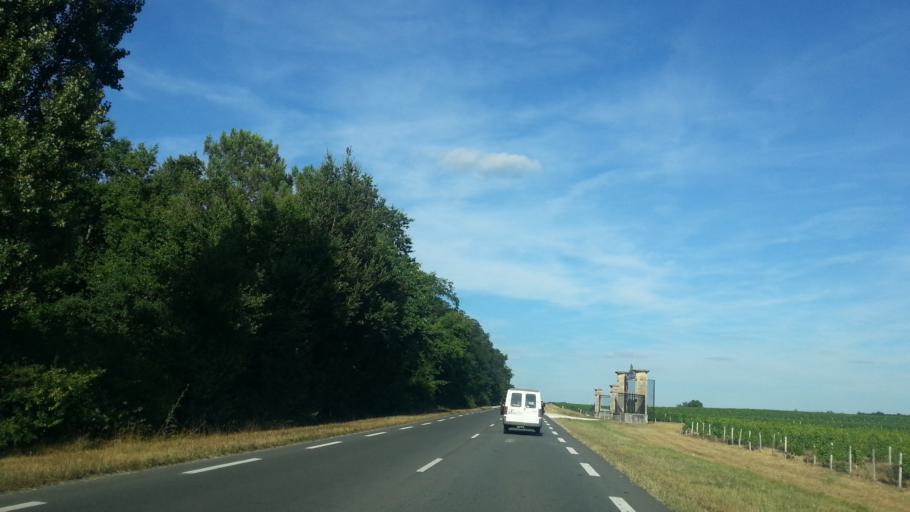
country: FR
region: Aquitaine
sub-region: Departement de la Gironde
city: Ayguemorte-les-Graves
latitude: 44.6971
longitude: -0.4776
